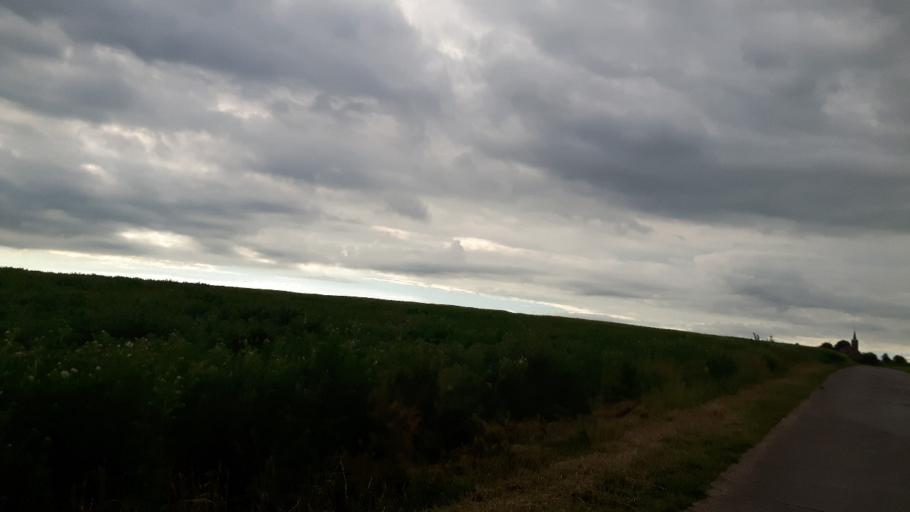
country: DE
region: Bavaria
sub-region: Regierungsbezirk Unterfranken
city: Stadtlauringen
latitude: 50.1783
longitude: 10.3635
